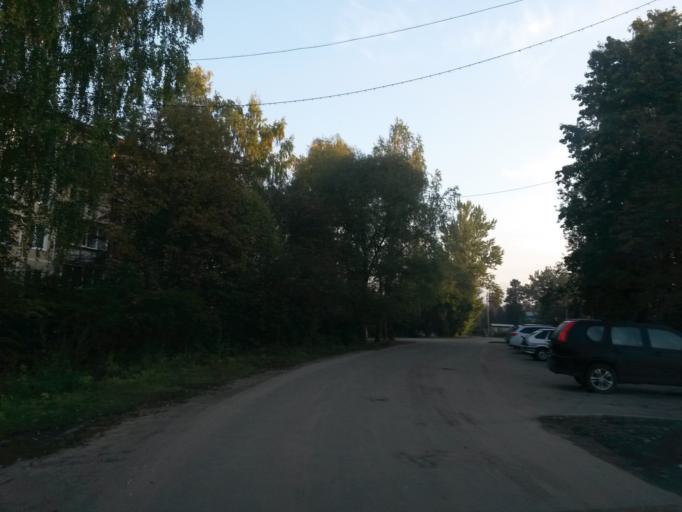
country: RU
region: Moskovskaya
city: Lyubuchany
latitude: 55.2444
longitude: 37.6287
